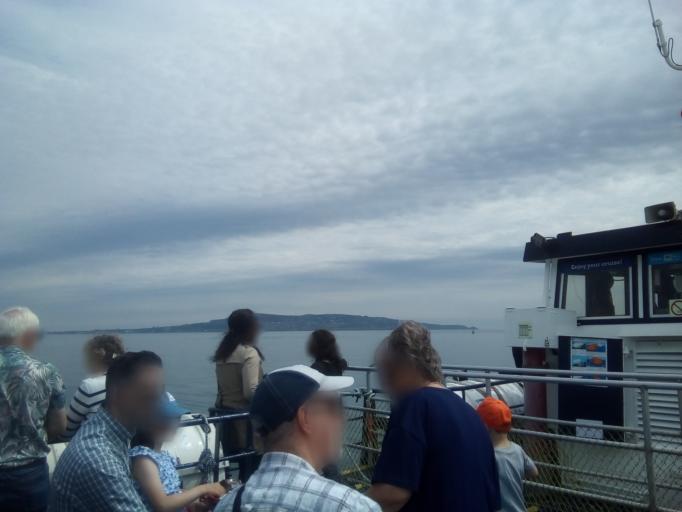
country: IE
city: Bayside
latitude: 53.3417
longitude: -6.1379
